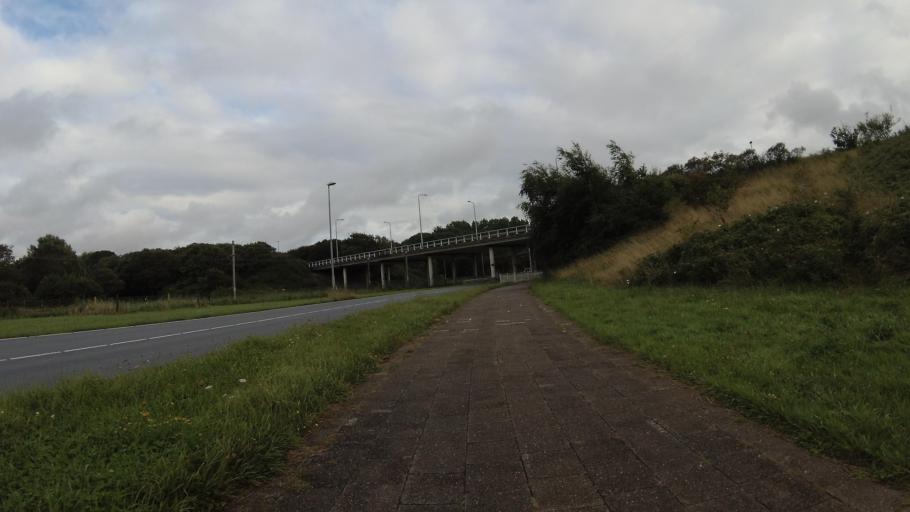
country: NL
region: North Holland
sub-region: Gemeente Den Helder
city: Den Helder
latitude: 52.9413
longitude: 4.7596
